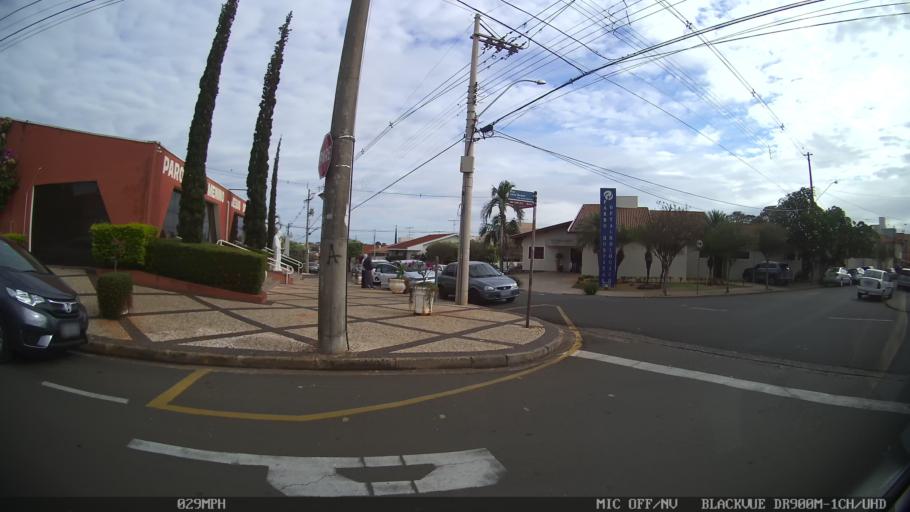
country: BR
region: Sao Paulo
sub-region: Sao Jose Do Rio Preto
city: Sao Jose do Rio Preto
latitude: -20.8314
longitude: -49.4004
